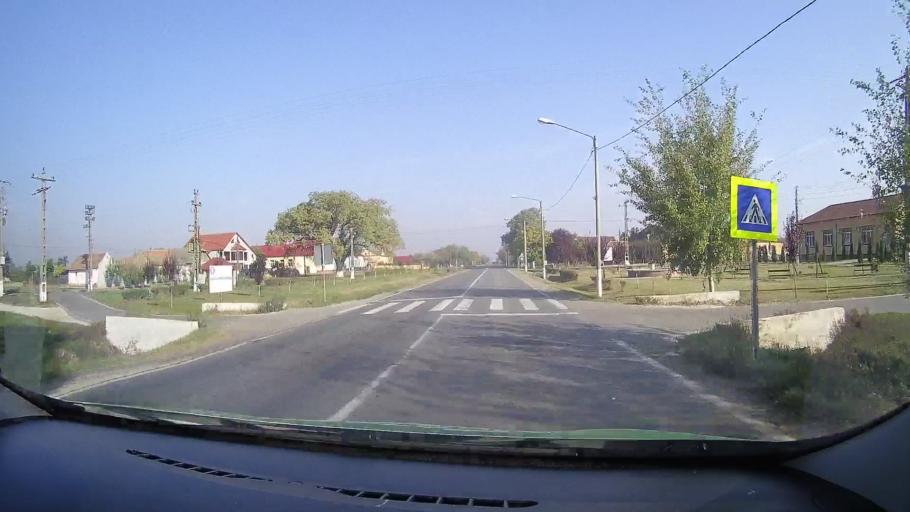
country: RO
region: Arad
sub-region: Comuna Pilu
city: Pilu
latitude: 46.5752
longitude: 21.3426
